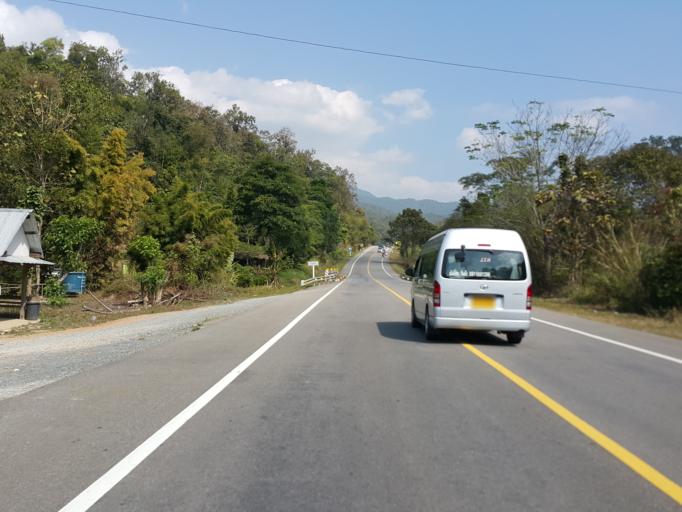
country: TH
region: Chiang Mai
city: Mae On
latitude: 19.0297
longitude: 99.3209
